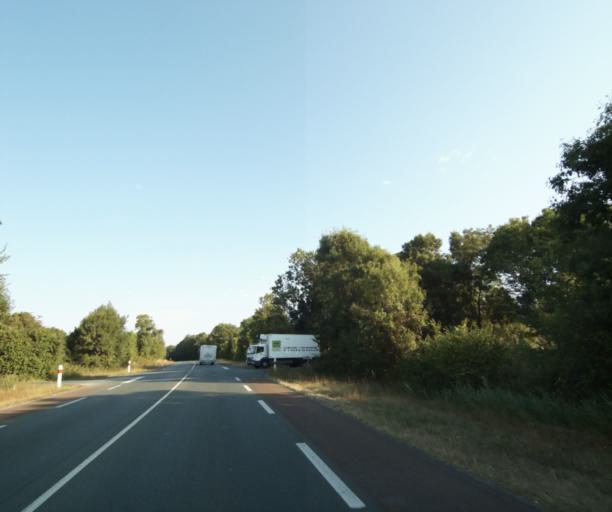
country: FR
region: Poitou-Charentes
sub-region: Departement de la Charente-Maritime
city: Cabariot
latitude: 45.9441
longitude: -0.8646
